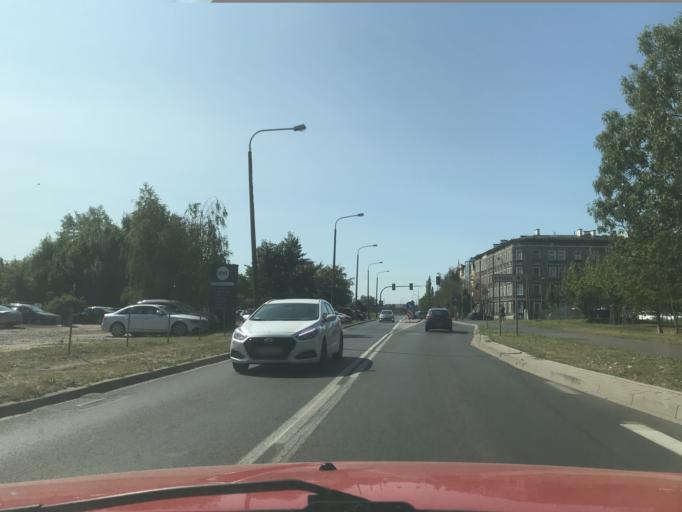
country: PL
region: Greater Poland Voivodeship
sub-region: Poznan
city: Poznan
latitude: 52.3886
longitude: 16.9239
